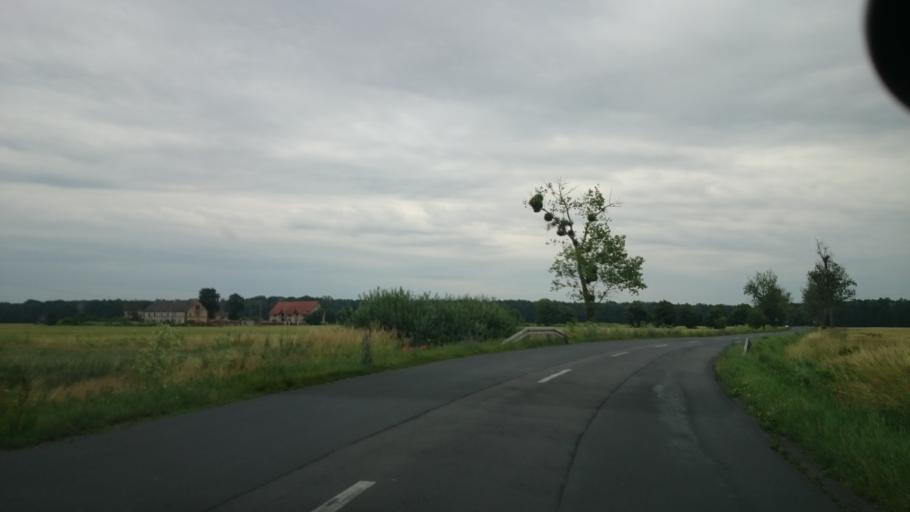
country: PL
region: Opole Voivodeship
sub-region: Powiat brzeski
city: Grodkow
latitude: 50.6734
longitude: 17.4157
